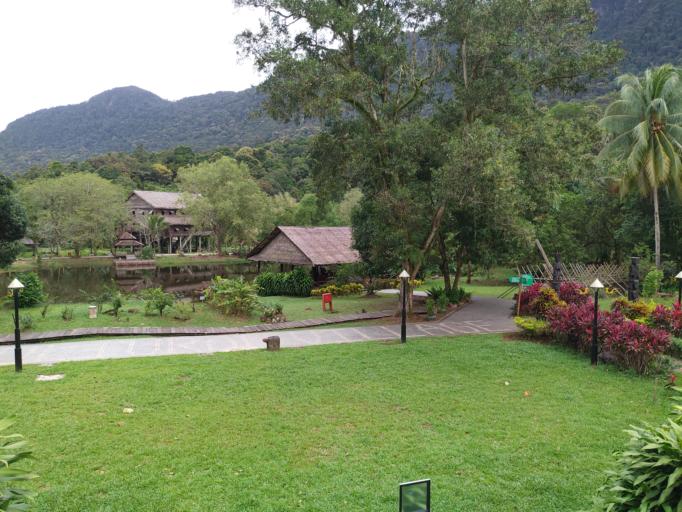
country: MY
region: Sarawak
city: Kuching
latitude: 1.7497
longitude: 110.3161
